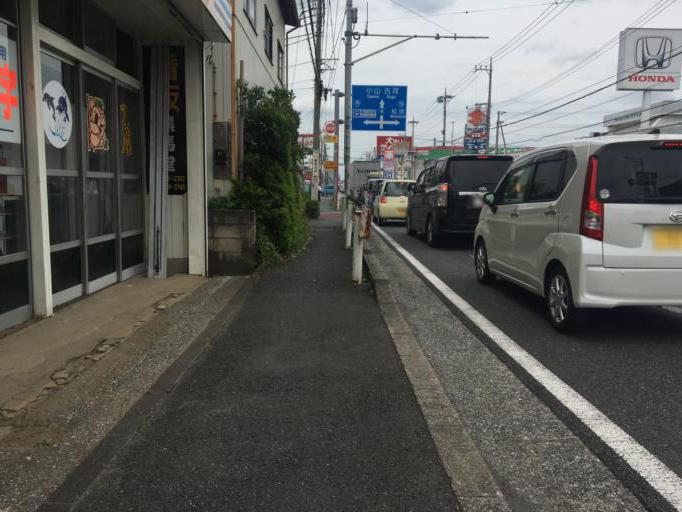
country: JP
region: Saitama
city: Kasukabe
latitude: 35.9710
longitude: 139.7675
